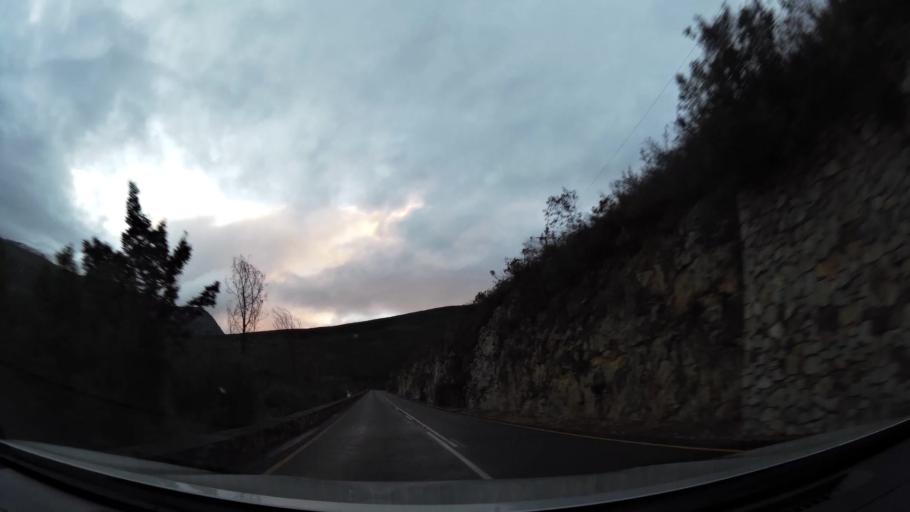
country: ZA
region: Western Cape
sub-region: Overberg District Municipality
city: Swellendam
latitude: -33.9806
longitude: 20.7100
